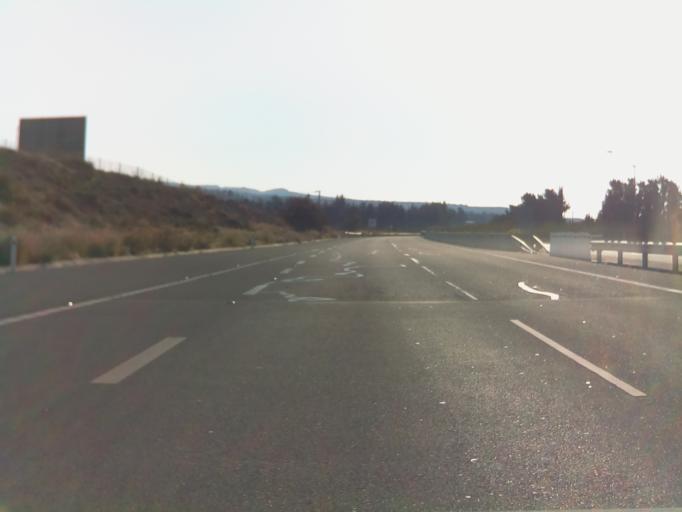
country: CY
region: Limassol
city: Pissouri
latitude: 34.7081
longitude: 32.5587
